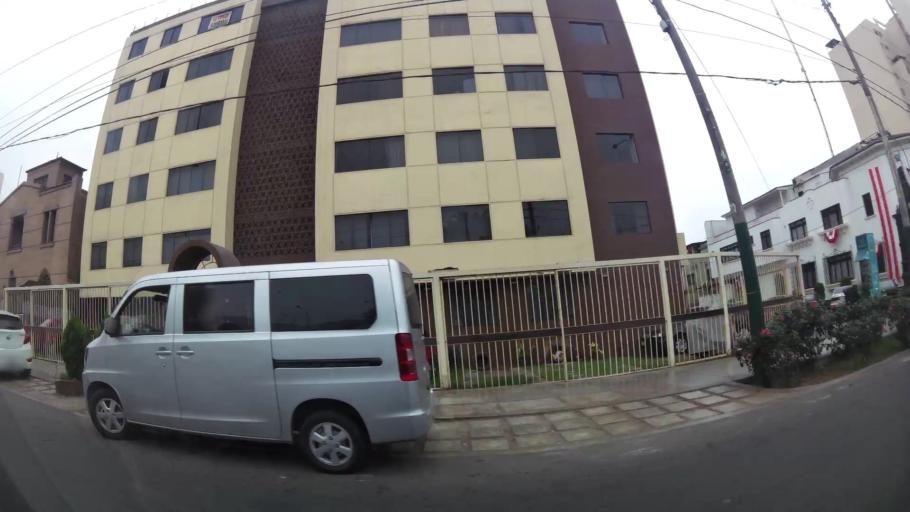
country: PE
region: Lima
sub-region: Lima
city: San Isidro
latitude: -12.0913
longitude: -77.0670
